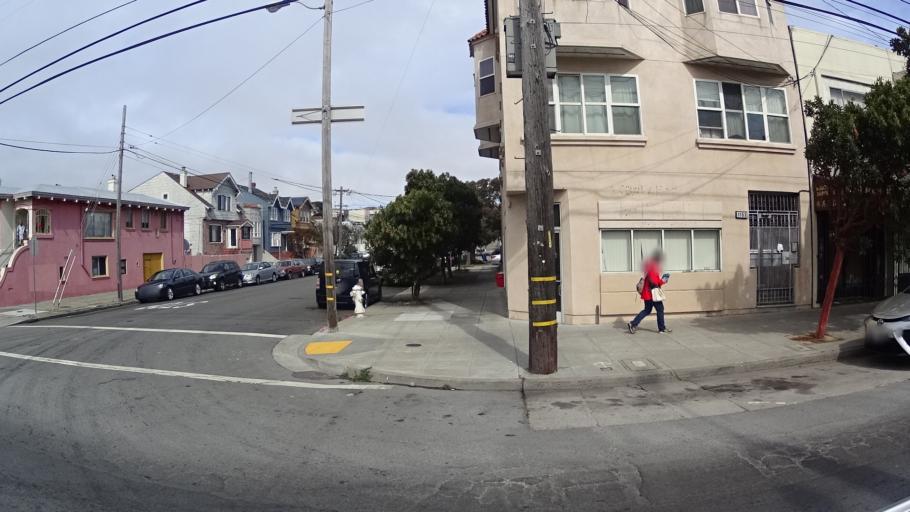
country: US
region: California
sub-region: San Mateo County
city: Daly City
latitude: 37.7146
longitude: -122.4369
